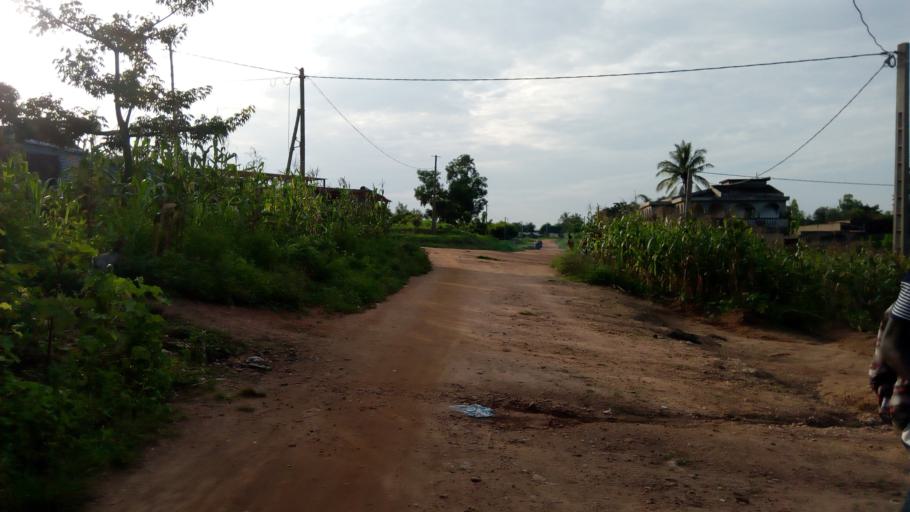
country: TG
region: Kara
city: Kara
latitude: 9.5613
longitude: 1.2077
